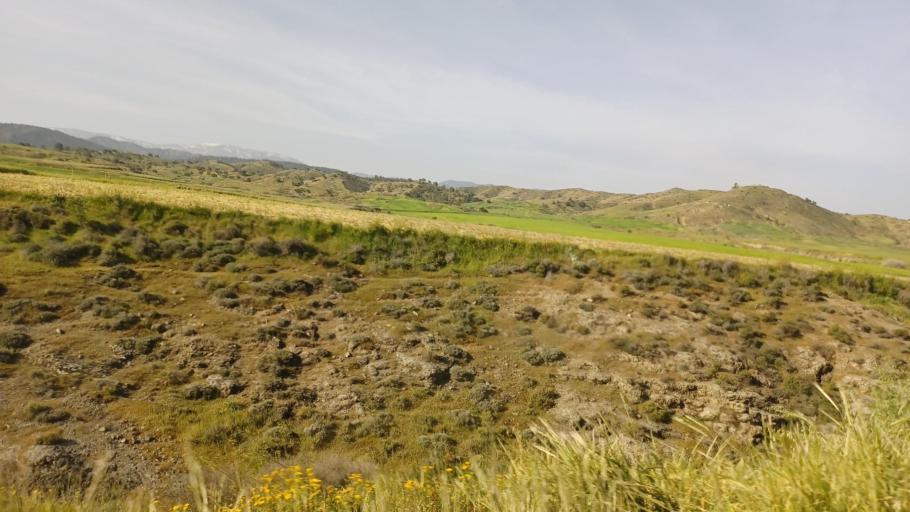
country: CY
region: Lefkosia
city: Lefka
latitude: 35.0890
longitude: 32.9484
